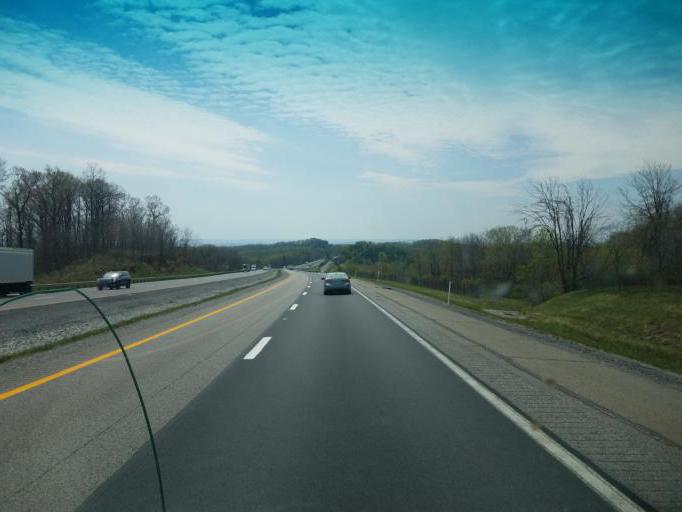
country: US
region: West Virginia
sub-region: Raleigh County
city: Shady Spring
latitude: 37.5625
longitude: -81.1132
